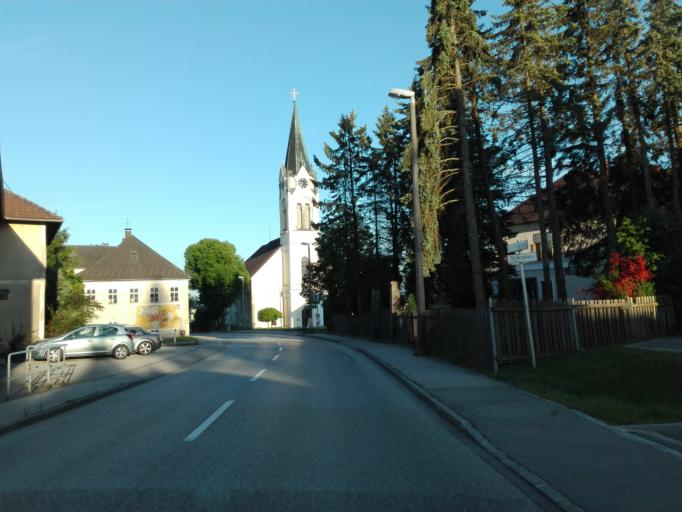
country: AT
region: Upper Austria
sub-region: Politischer Bezirk Linz-Land
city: Horsching
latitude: 48.2557
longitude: 14.1649
